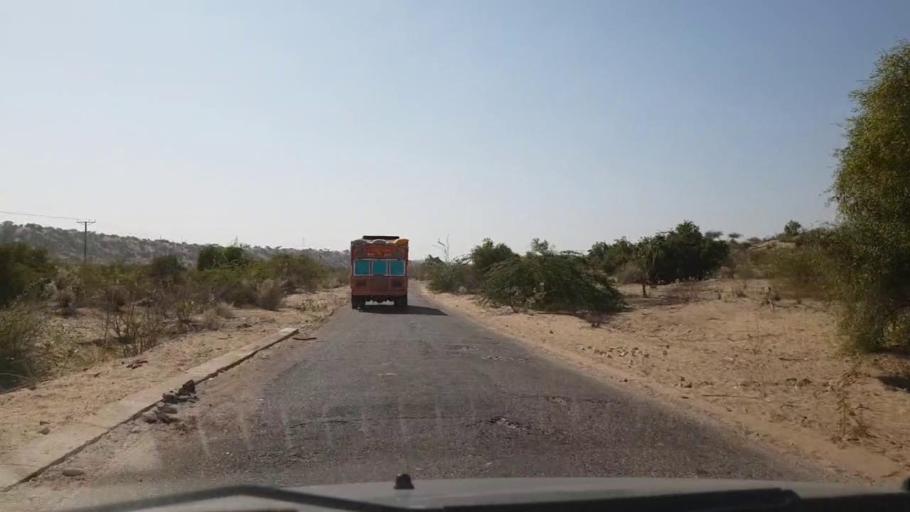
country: PK
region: Sindh
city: Diplo
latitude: 24.5377
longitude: 69.6419
